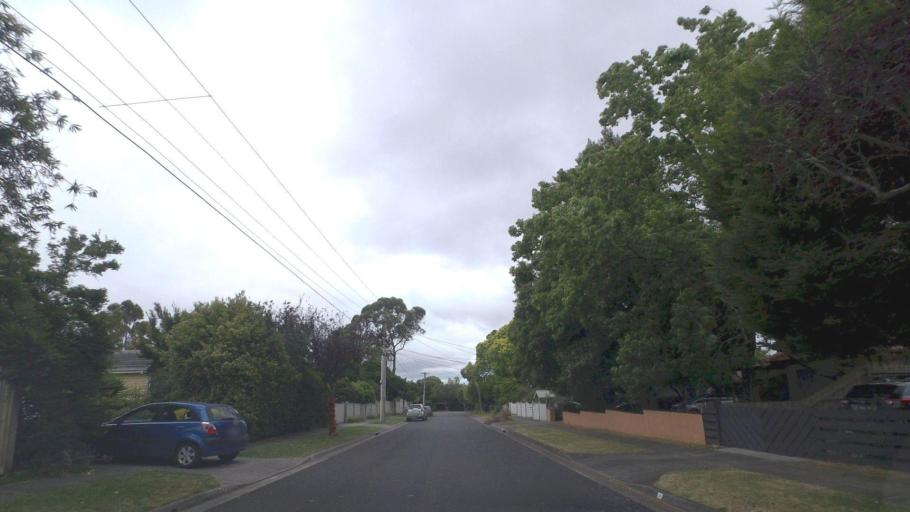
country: AU
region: Victoria
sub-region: Knox
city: Knoxfield
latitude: -37.8753
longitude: 145.2615
